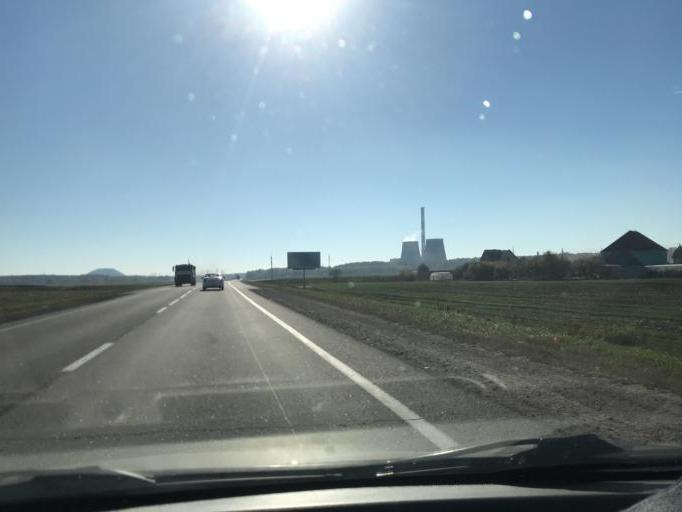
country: BY
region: Gomel
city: Kastsyukowka
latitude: 52.4647
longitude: 30.8244
